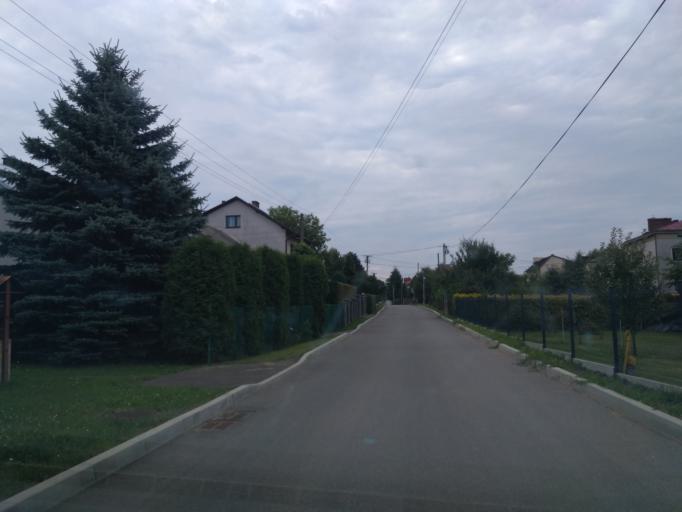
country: PL
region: Subcarpathian Voivodeship
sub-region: Powiat sanocki
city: Sanok
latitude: 49.5693
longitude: 22.1695
